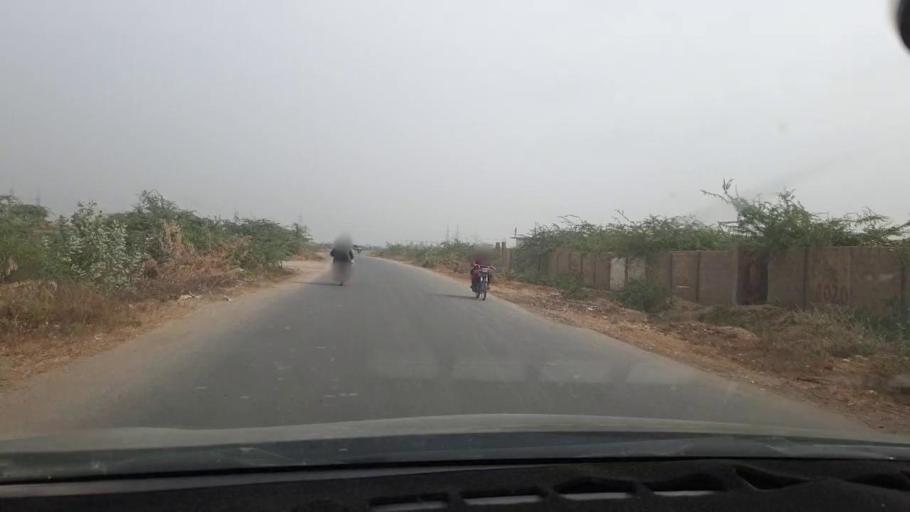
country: PK
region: Sindh
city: Malir Cantonment
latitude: 24.9137
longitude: 67.2725
